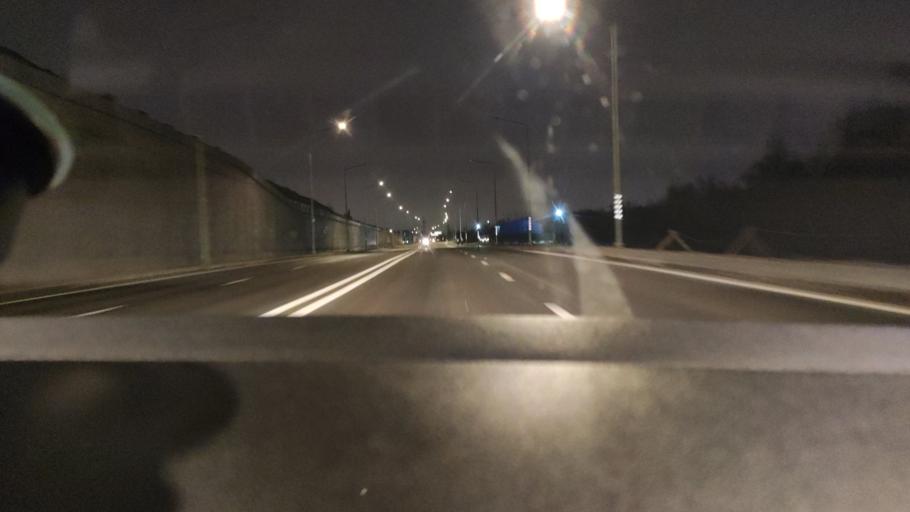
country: RU
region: Moskovskaya
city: Mosrentgen
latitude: 55.6103
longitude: 37.4343
